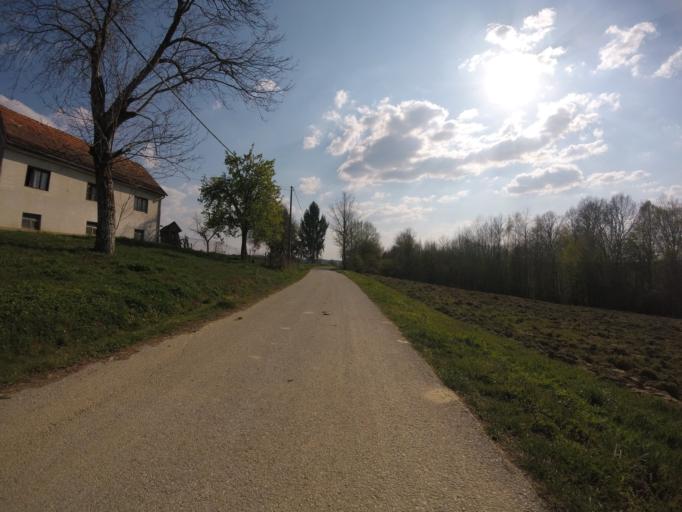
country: HR
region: Sisacko-Moslavacka
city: Glina
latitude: 45.4971
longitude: 16.0046
